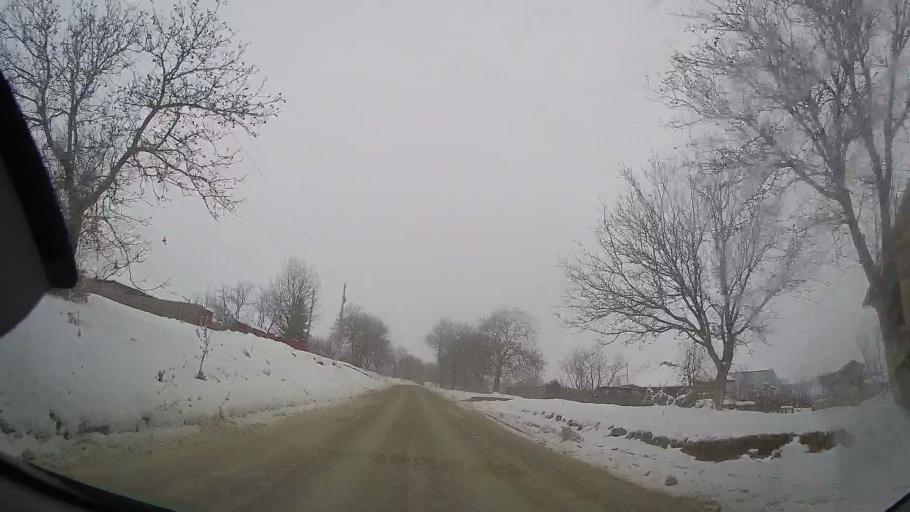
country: RO
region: Vaslui
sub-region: Comuna Todiresti
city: Todiresti
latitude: 46.8741
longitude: 27.3789
